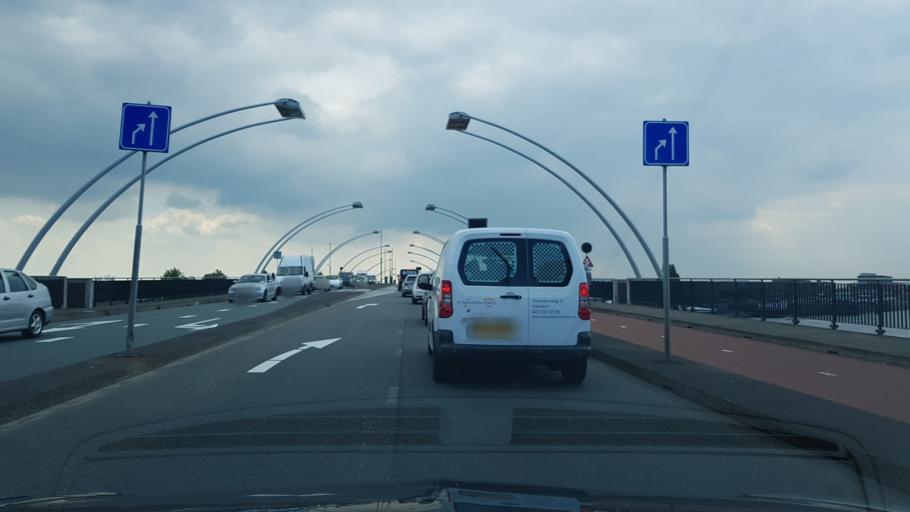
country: NL
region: North Holland
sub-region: Gemeente Haarlem
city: Haarlem
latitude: 52.4036
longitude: 4.6561
